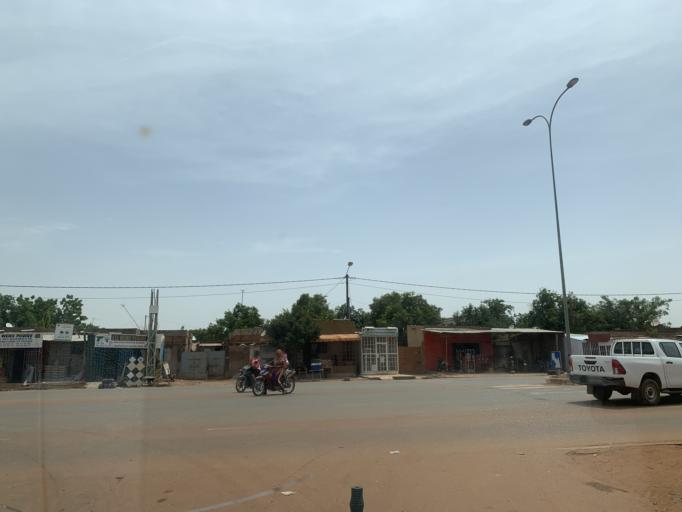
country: BF
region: Centre
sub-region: Kadiogo Province
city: Ouagadougou
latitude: 12.3393
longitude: -1.5145
